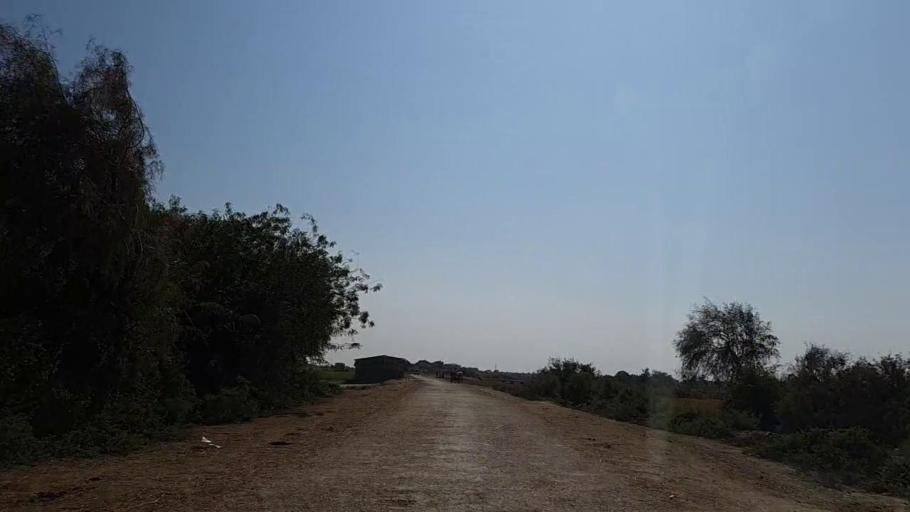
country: PK
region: Sindh
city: Chuhar Jamali
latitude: 24.4584
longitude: 68.1150
